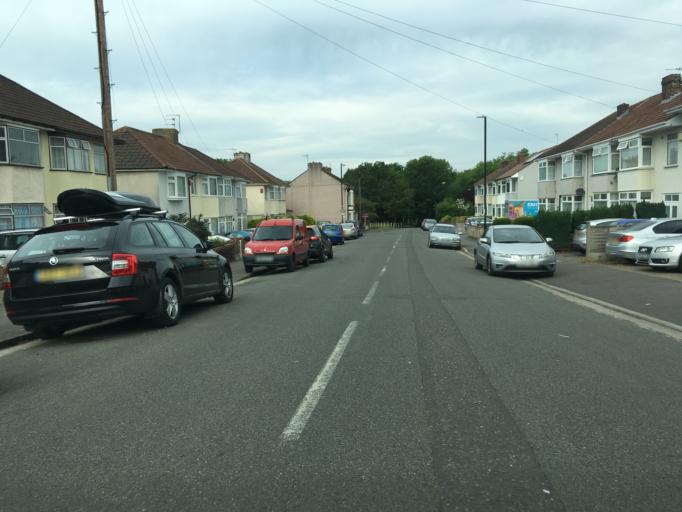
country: GB
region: England
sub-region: South Gloucestershire
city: Kingswood
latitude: 51.4730
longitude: -2.5389
